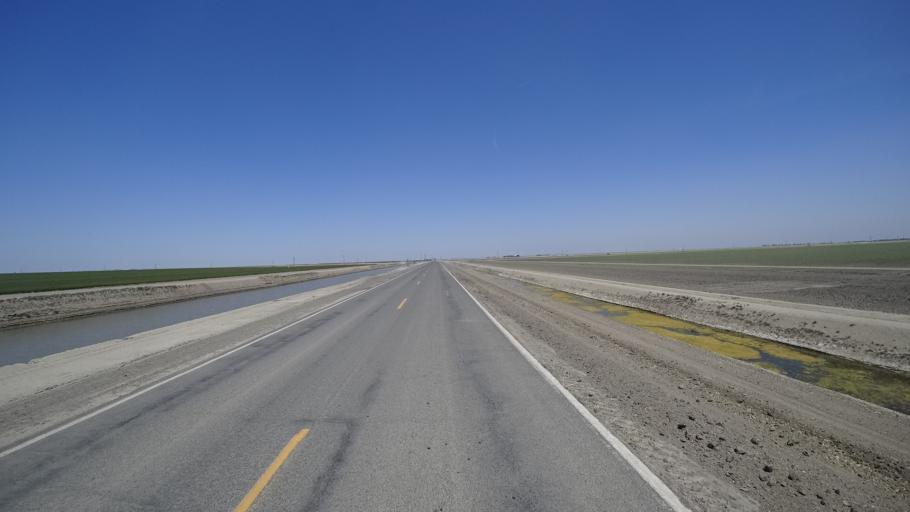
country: US
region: California
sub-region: Kings County
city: Corcoran
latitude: 36.0752
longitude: -119.6439
